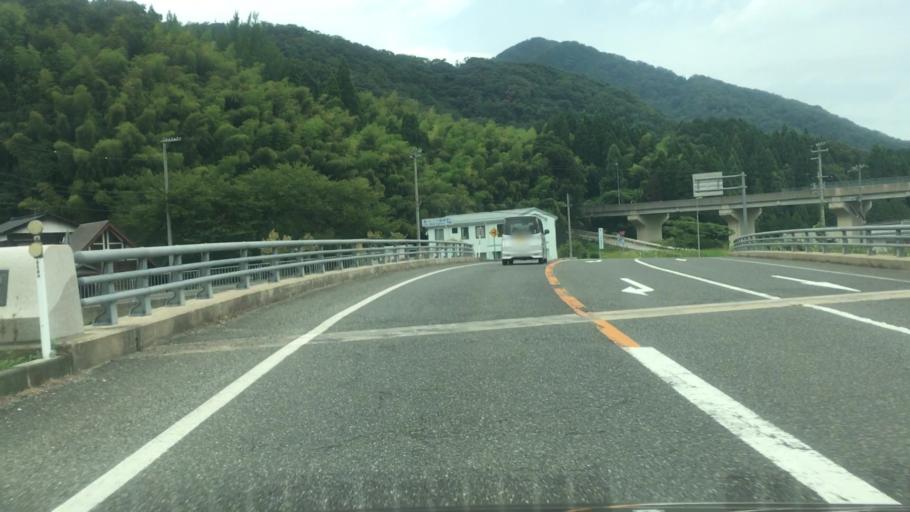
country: JP
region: Hyogo
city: Toyooka
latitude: 35.6273
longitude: 134.6786
